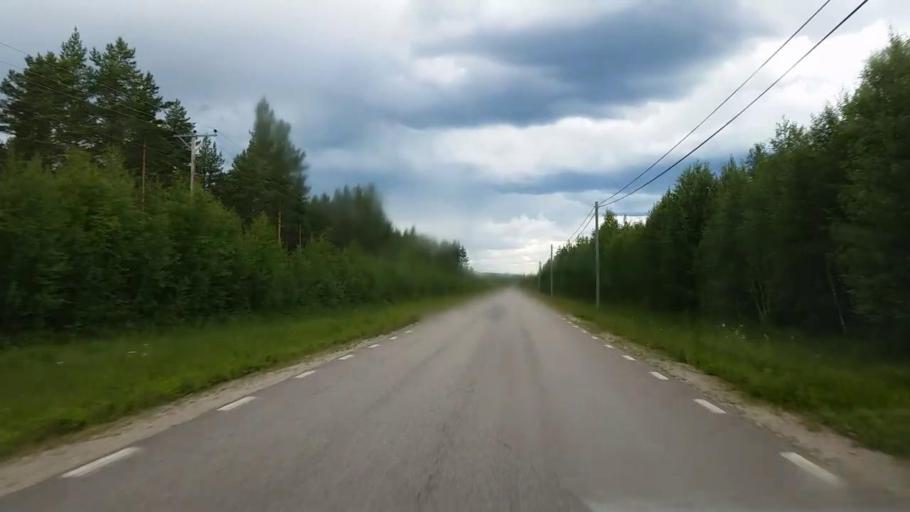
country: SE
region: Gaevleborg
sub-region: Ovanakers Kommun
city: Edsbyn
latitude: 61.4420
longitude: 15.8891
